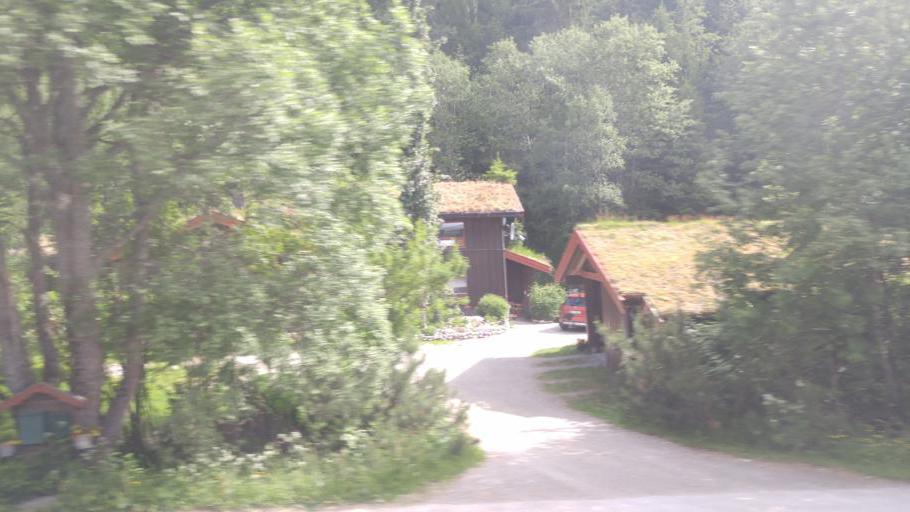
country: NO
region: Sor-Trondelag
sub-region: Midtre Gauldal
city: Storen
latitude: 63.0378
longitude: 10.2979
